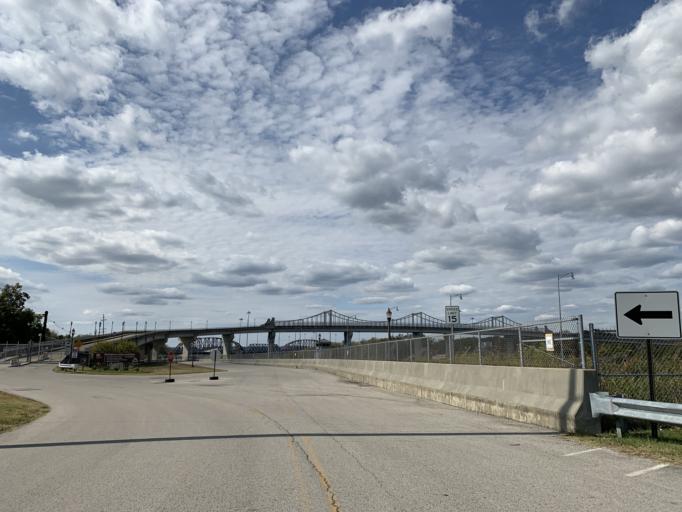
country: US
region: Indiana
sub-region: Clark County
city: Clarksville
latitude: 38.2760
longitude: -85.7884
